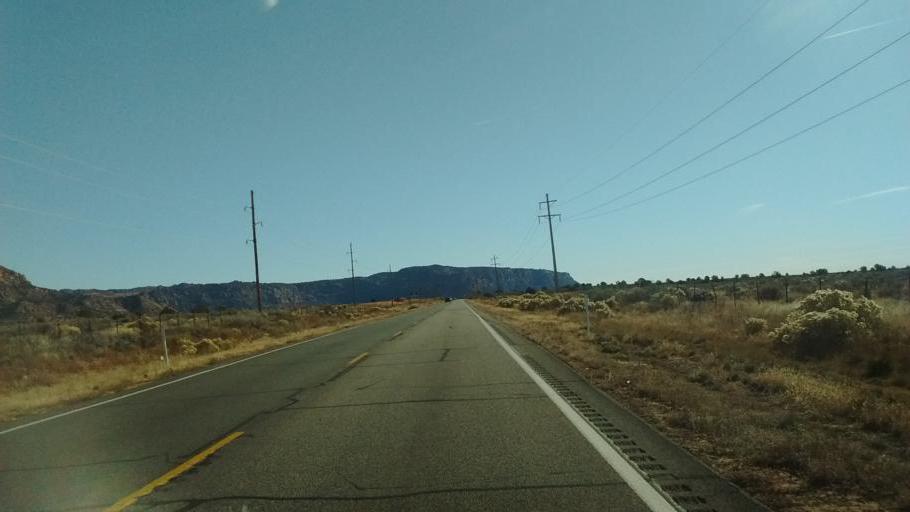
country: US
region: Arizona
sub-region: Mohave County
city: Colorado City
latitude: 37.0121
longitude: -113.0189
